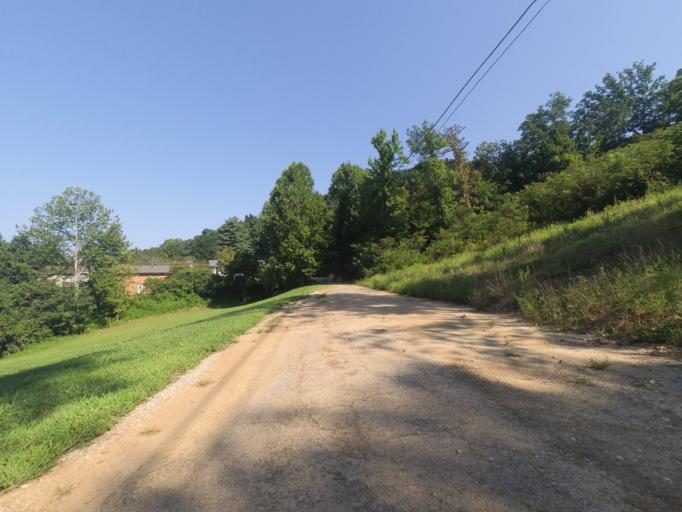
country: US
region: West Virginia
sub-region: Cabell County
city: Huntington
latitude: 38.4321
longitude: -82.4515
